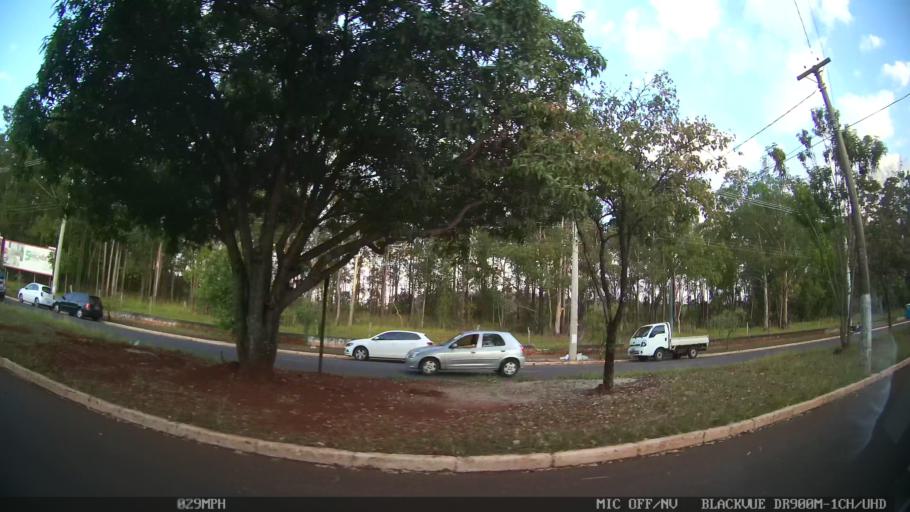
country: BR
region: Sao Paulo
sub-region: Ribeirao Preto
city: Ribeirao Preto
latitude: -21.1575
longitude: -47.7849
